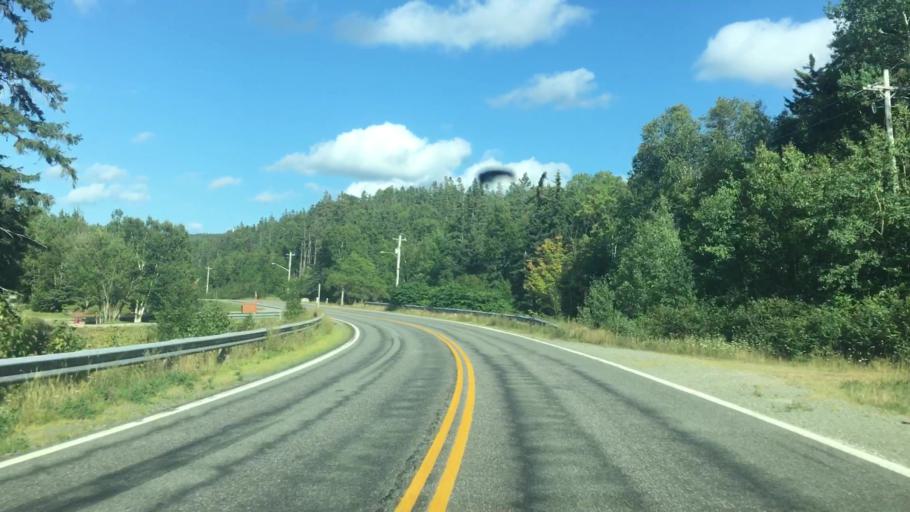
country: CA
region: Nova Scotia
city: Sydney
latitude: 45.8672
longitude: -60.6152
